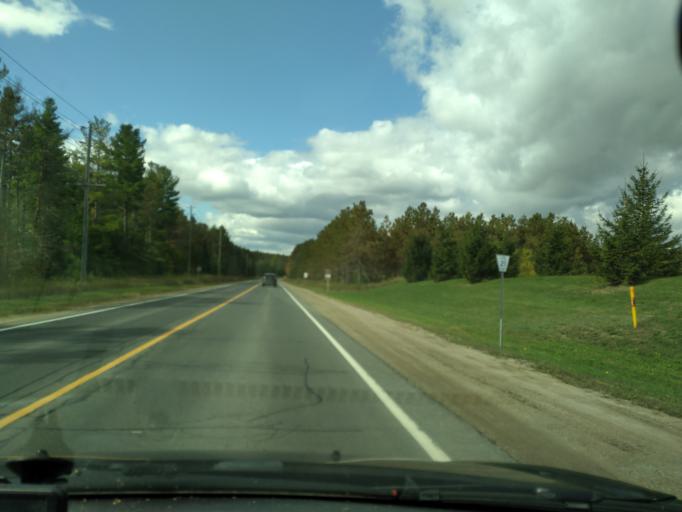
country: CA
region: Ontario
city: Angus
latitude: 44.2534
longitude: -79.8007
